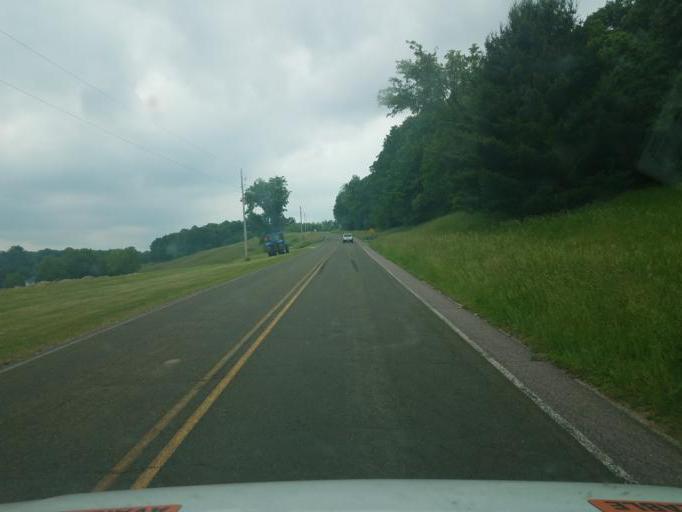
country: US
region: Wisconsin
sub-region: Juneau County
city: Elroy
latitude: 43.6541
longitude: -90.2397
